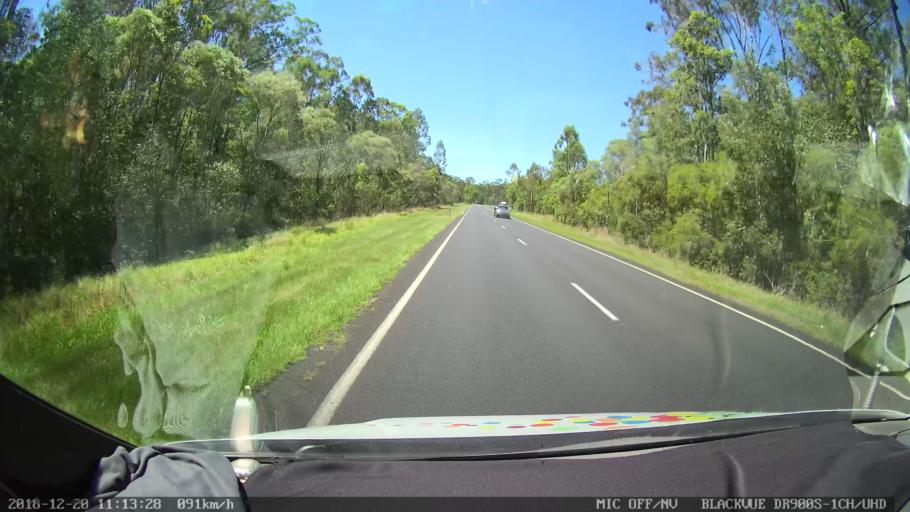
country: AU
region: New South Wales
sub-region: Richmond Valley
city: Casino
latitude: -28.9881
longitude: 153.0108
